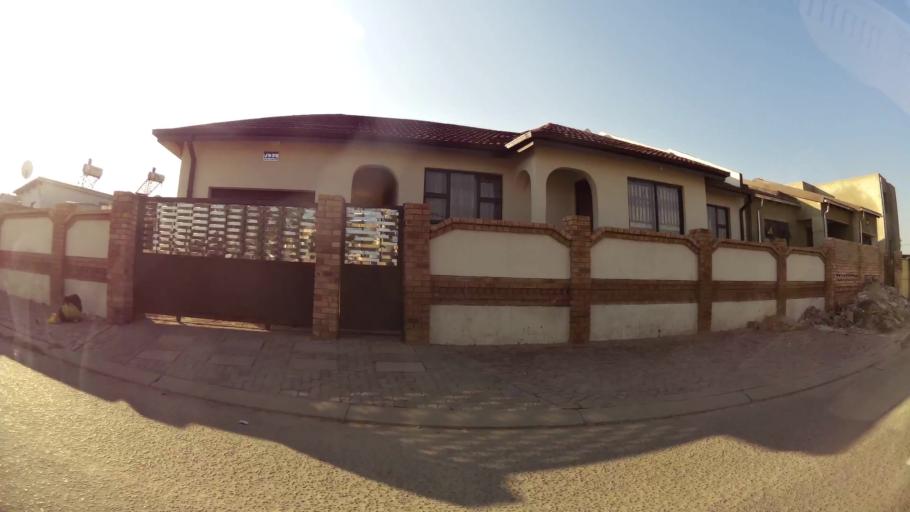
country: ZA
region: Gauteng
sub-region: City of Johannesburg Metropolitan Municipality
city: Modderfontein
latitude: -26.0921
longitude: 28.1091
